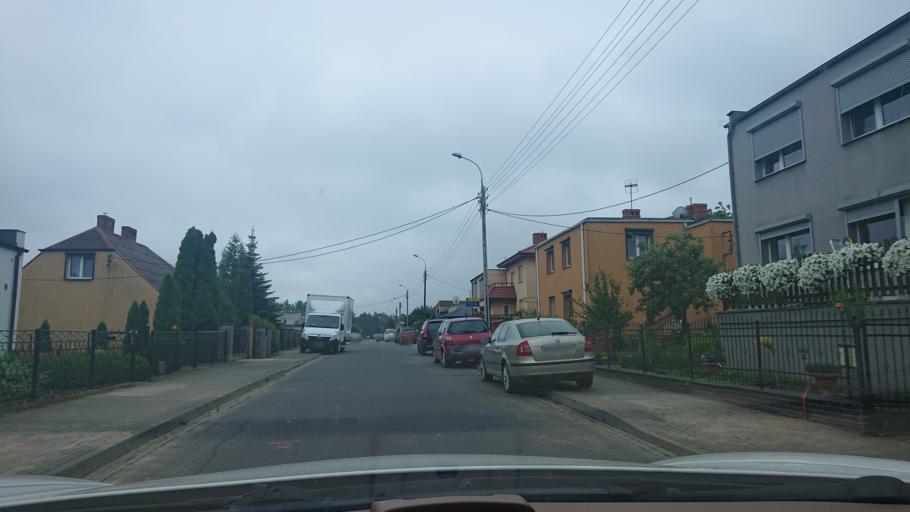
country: PL
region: Greater Poland Voivodeship
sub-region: Powiat gnieznienski
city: Gniezno
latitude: 52.5111
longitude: 17.5984
